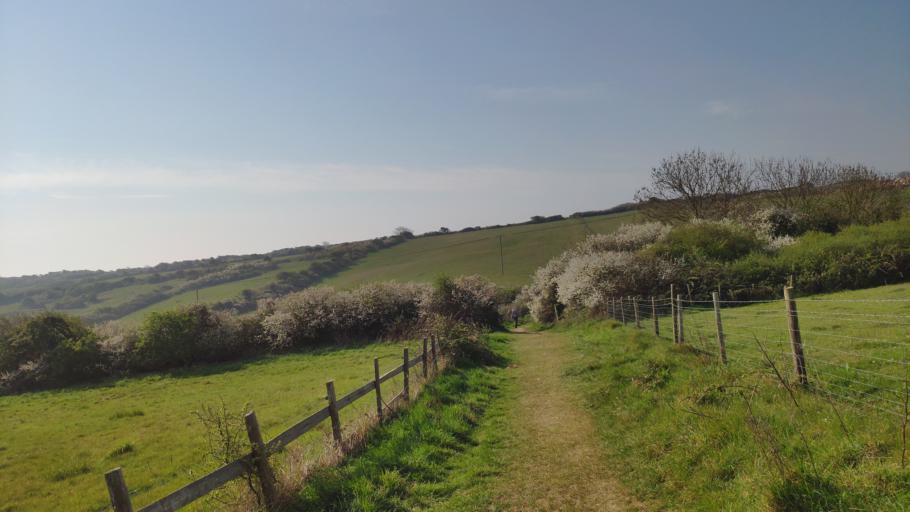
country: GB
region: England
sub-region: Dorset
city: Swanage
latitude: 50.6007
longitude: -1.9665
